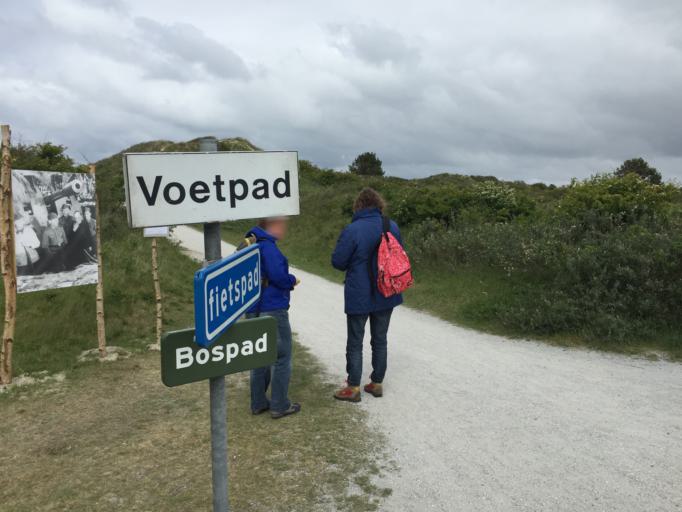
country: NL
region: Friesland
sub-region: Gemeente Schiermonnikoog
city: Schiermonnikoog
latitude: 53.4925
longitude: 6.1547
